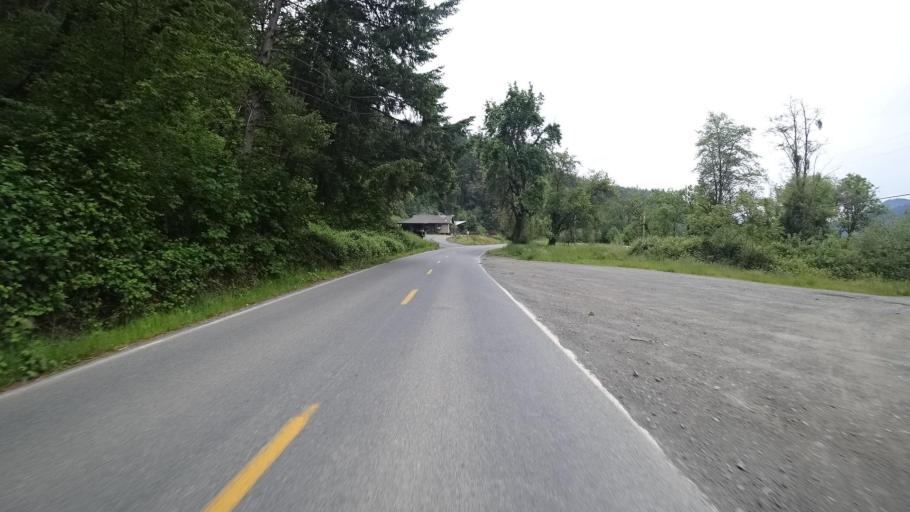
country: US
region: California
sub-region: Humboldt County
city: Willow Creek
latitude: 41.0606
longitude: -123.6928
